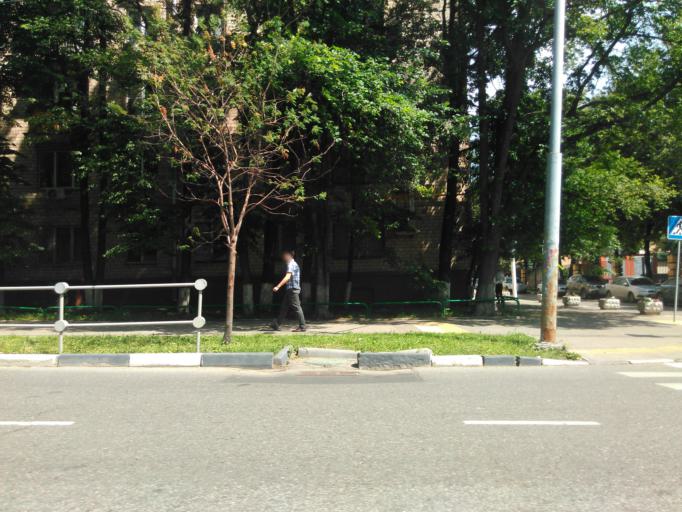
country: RU
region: Moskovskaya
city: Semenovskoye
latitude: 55.6890
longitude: 37.5320
